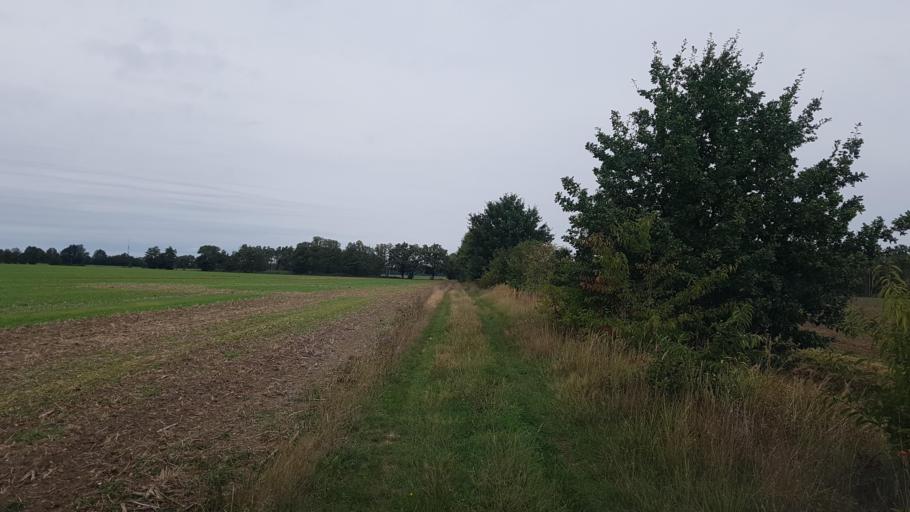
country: DE
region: Brandenburg
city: Schonewalde
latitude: 51.6412
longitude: 13.6061
